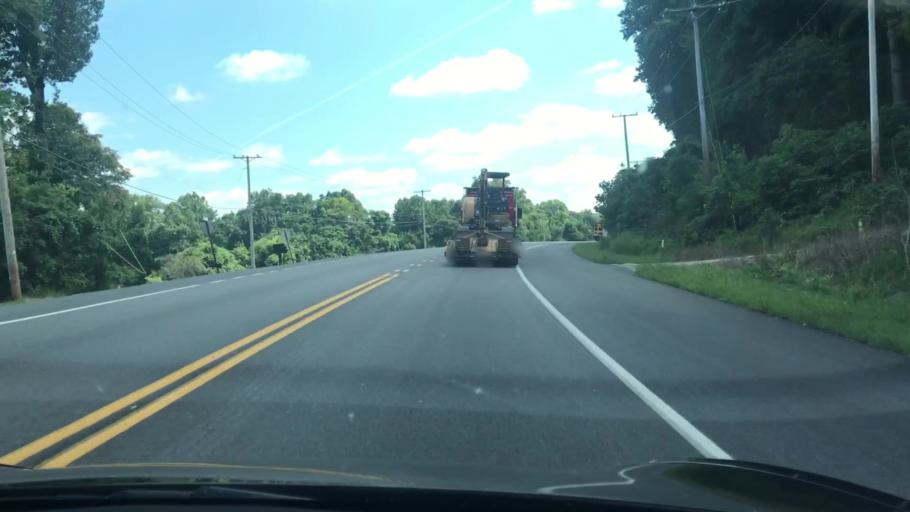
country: US
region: Pennsylvania
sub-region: York County
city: Valley Green
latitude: 40.1337
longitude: -76.8072
